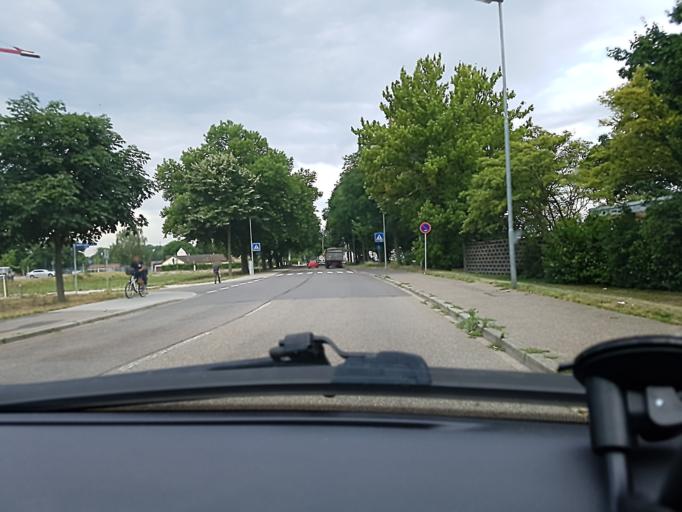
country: DE
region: Baden-Wuerttemberg
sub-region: Freiburg Region
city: Kehl
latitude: 48.5636
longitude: 7.8176
